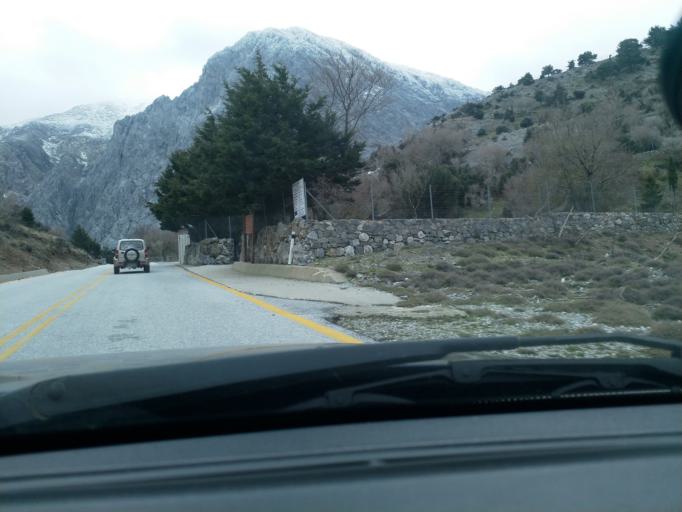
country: GR
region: Crete
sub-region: Nomos Chanias
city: Perivolia
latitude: 35.3097
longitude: 23.9176
